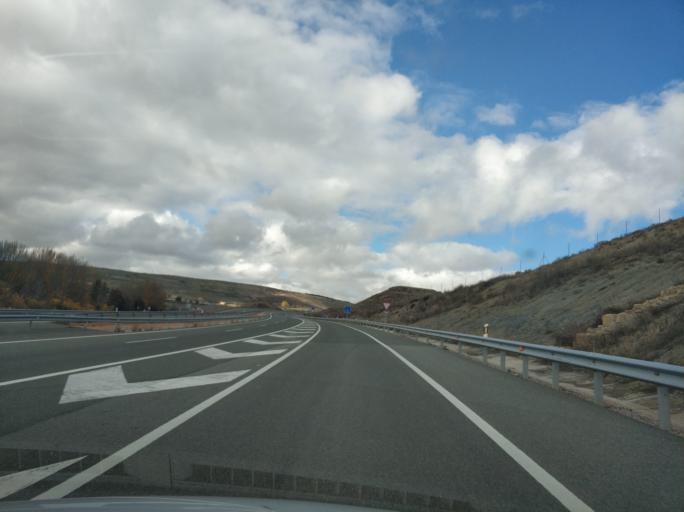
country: ES
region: Castille and Leon
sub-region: Provincia de Soria
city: Medinaceli
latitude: 41.1753
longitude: -2.4227
